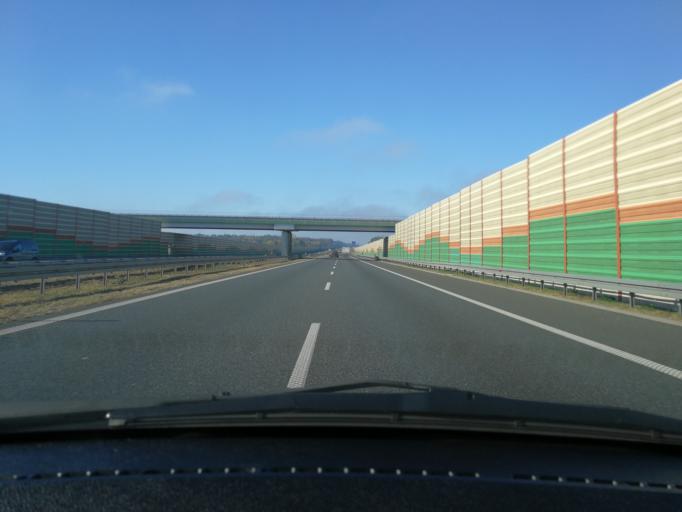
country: PL
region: Lodz Voivodeship
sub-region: Powiat skierniewicki
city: Bolimow
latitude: 52.0599
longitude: 20.1534
